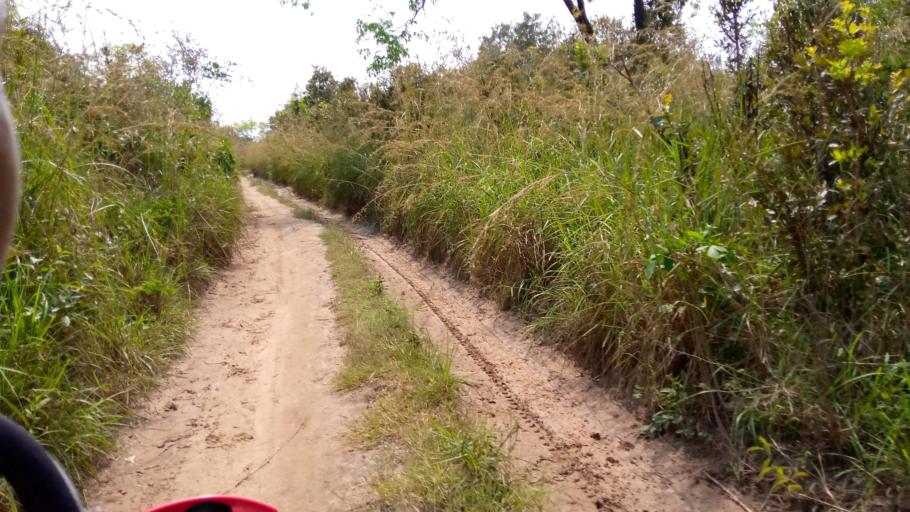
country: CD
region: Bandundu
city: Bandundu
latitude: -4.1331
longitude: 17.4159
